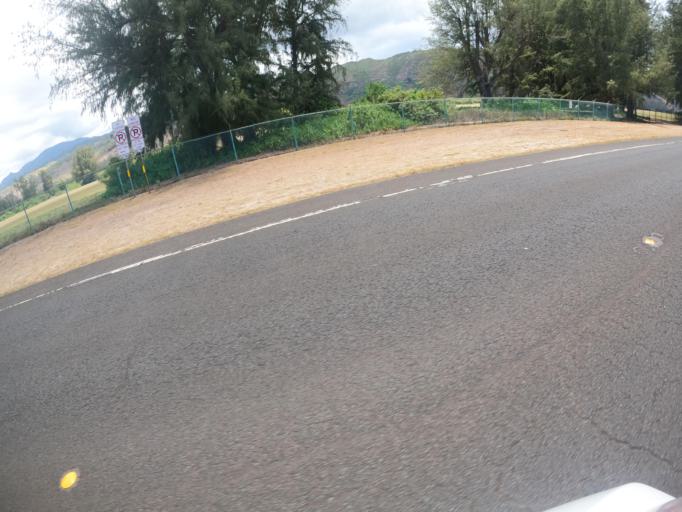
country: US
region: Hawaii
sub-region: Honolulu County
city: Mokuleia
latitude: 21.5812
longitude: -158.1916
